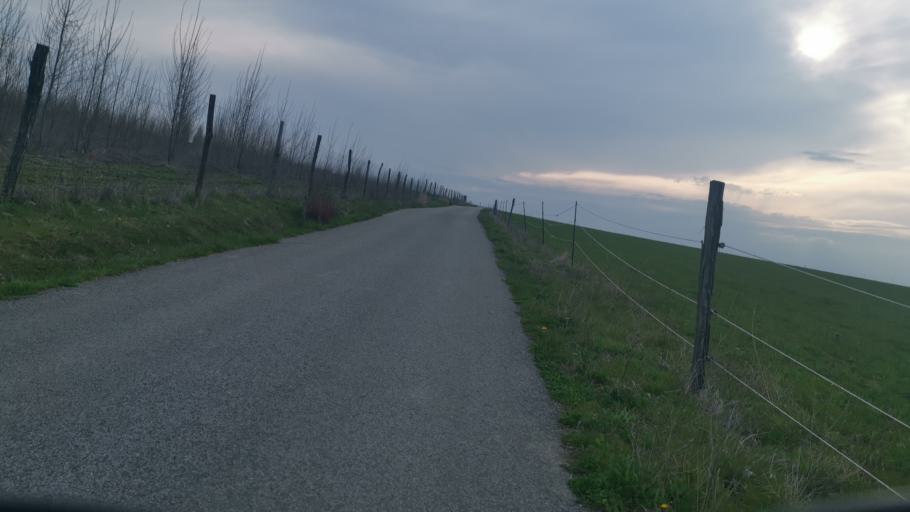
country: CZ
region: South Moravian
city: Petrov
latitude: 48.8450
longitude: 17.2950
